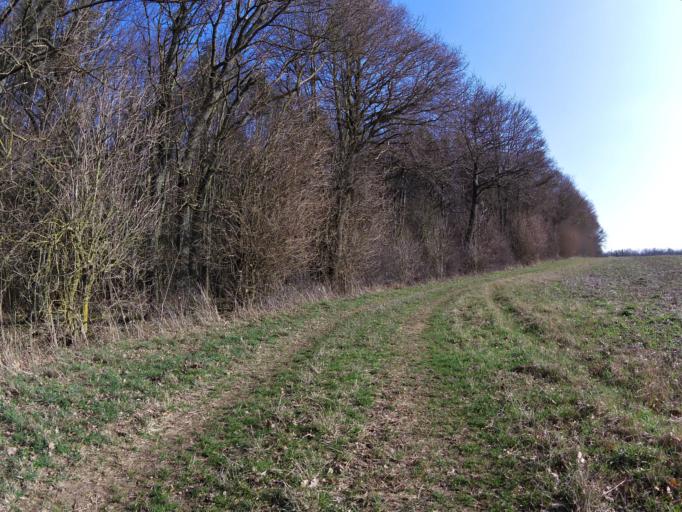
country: DE
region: Bavaria
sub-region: Regierungsbezirk Unterfranken
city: Rottendorf
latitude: 49.8211
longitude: 10.0398
